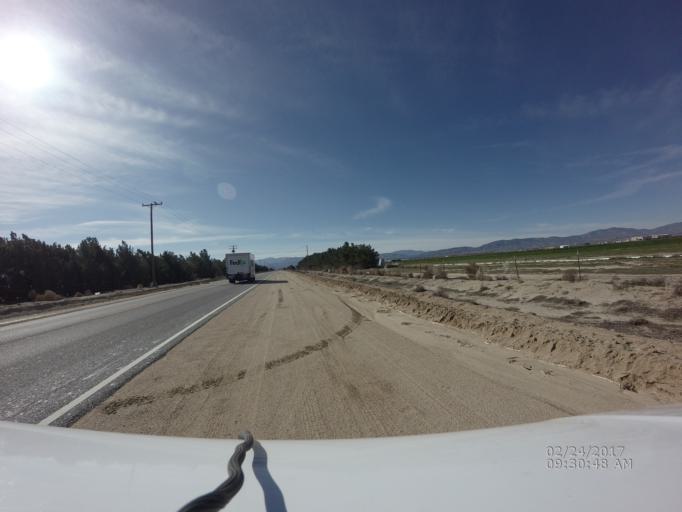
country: US
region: California
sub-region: Los Angeles County
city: Palmdale
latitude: 34.6237
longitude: -118.0410
